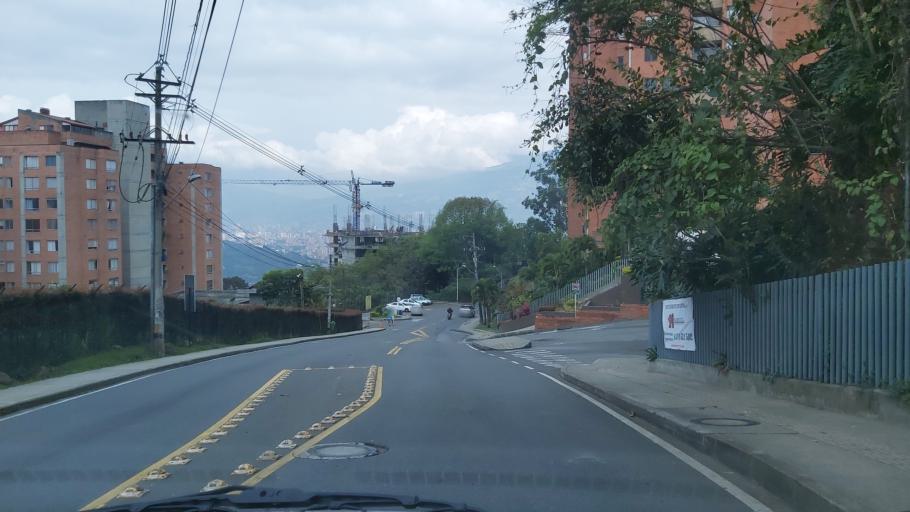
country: CO
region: Antioquia
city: Medellin
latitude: 6.2276
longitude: -75.5623
